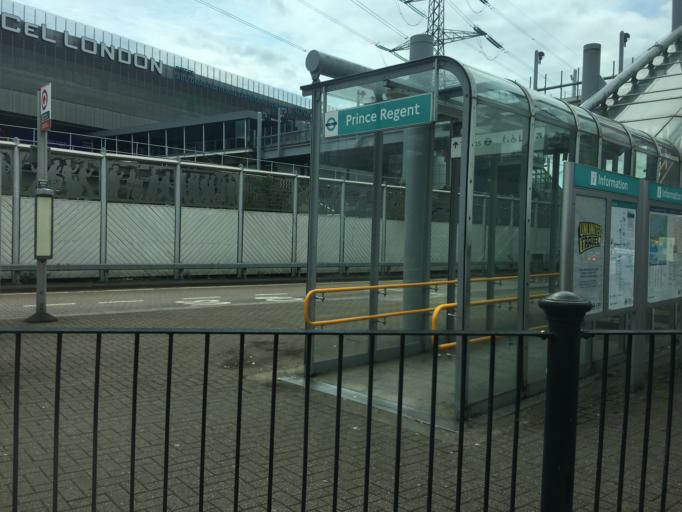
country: GB
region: England
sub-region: Greater London
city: East Ham
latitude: 51.5096
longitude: 0.0350
